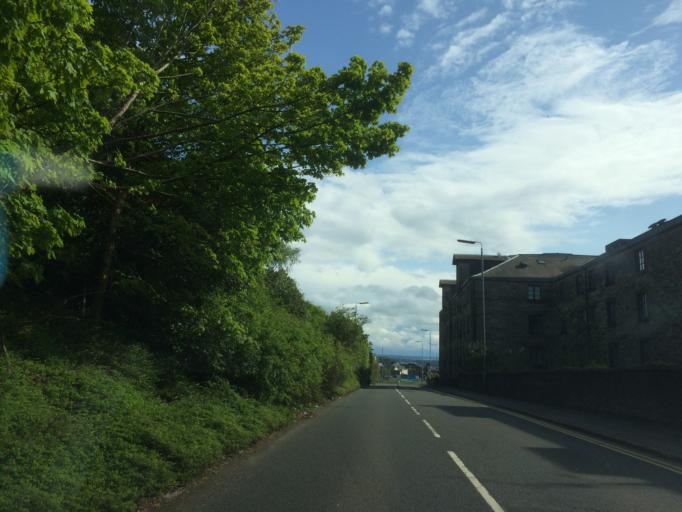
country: GB
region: Scotland
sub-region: Glasgow City
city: Glasgow
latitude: 55.8730
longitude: -4.2571
